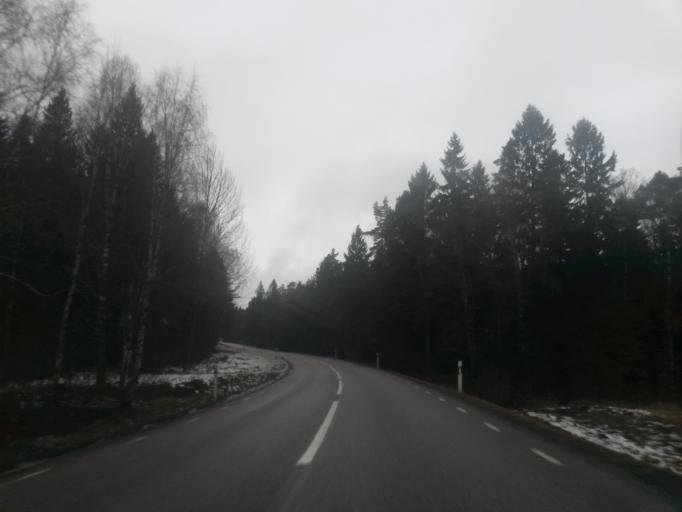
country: SE
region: Vaestra Goetaland
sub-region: Alingsas Kommun
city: Sollebrunn
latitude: 58.1292
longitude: 12.4965
